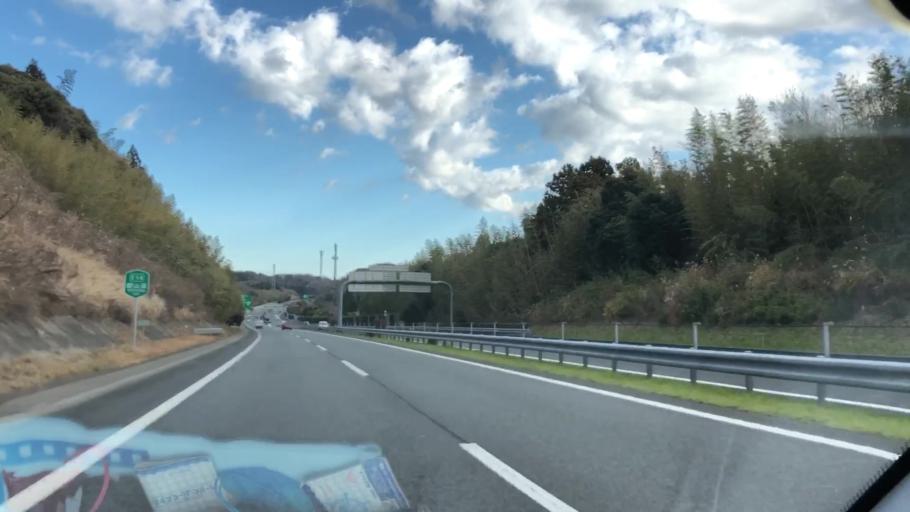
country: JP
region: Chiba
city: Kisarazu
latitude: 35.3588
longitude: 139.9544
